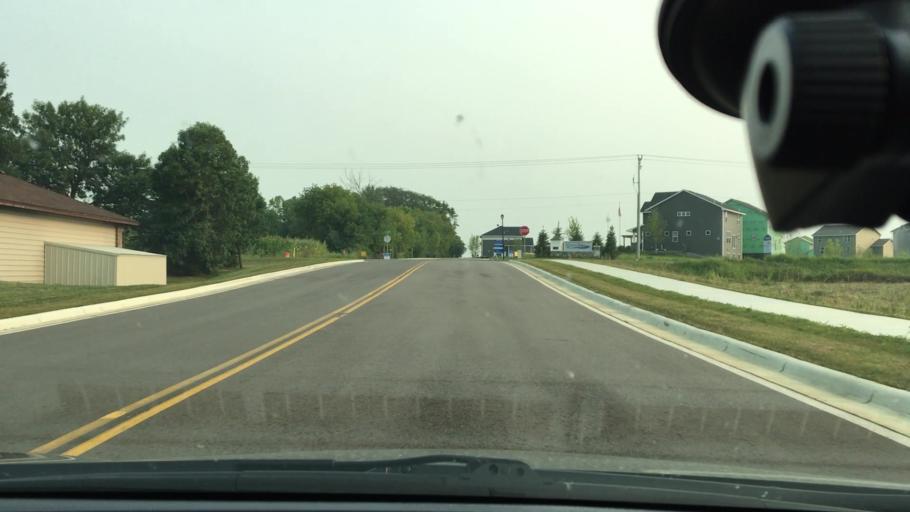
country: US
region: Minnesota
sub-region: Wright County
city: Saint Michael
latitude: 45.2109
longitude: -93.6292
